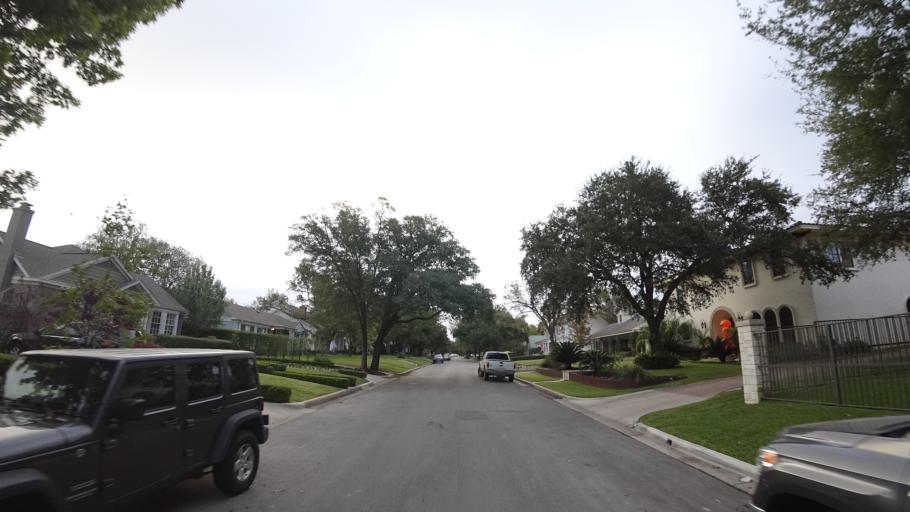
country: US
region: Texas
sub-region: Travis County
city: Austin
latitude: 30.2981
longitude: -97.7564
